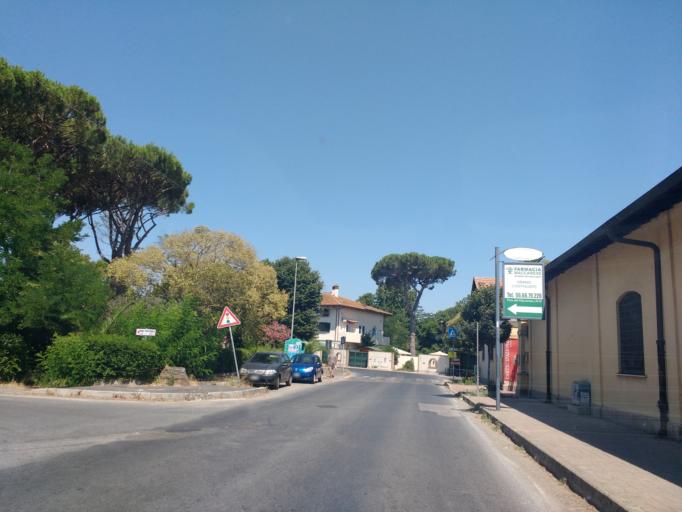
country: IT
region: Latium
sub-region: Citta metropolitana di Roma Capitale
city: Maccarese
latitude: 41.8773
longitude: 12.2148
